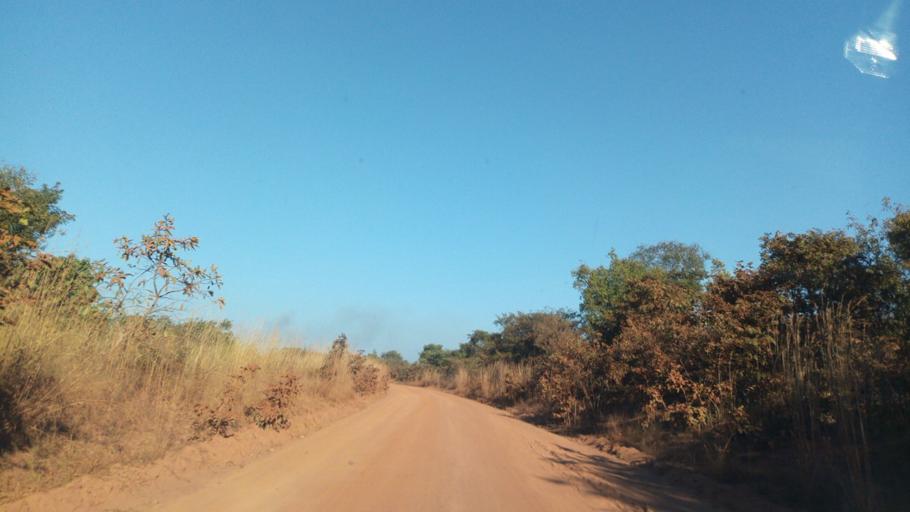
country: ZM
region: Luapula
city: Mwense
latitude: -10.4861
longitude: 28.4907
